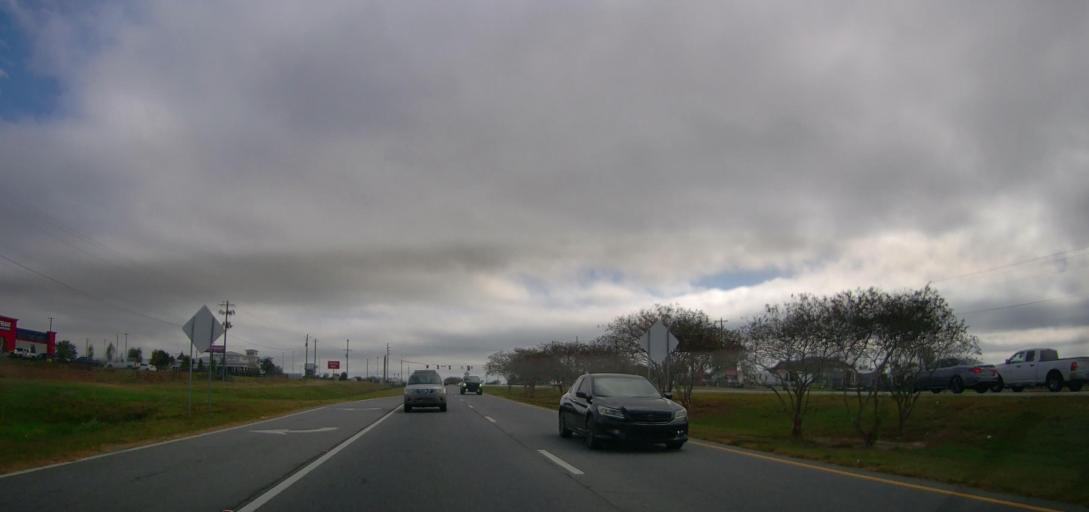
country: US
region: Georgia
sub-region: Colquitt County
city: Moultrie
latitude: 31.1953
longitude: -83.7666
